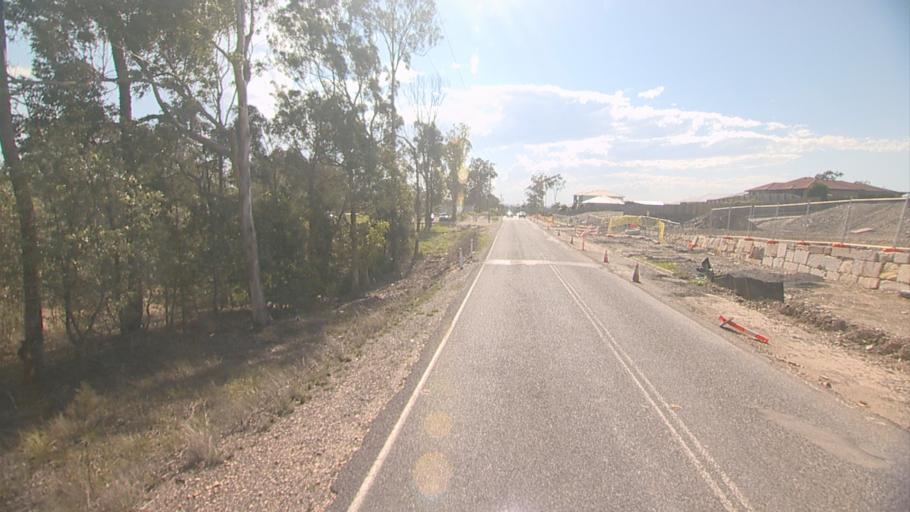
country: AU
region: Queensland
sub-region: Logan
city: Waterford West
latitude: -27.7204
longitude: 153.1570
